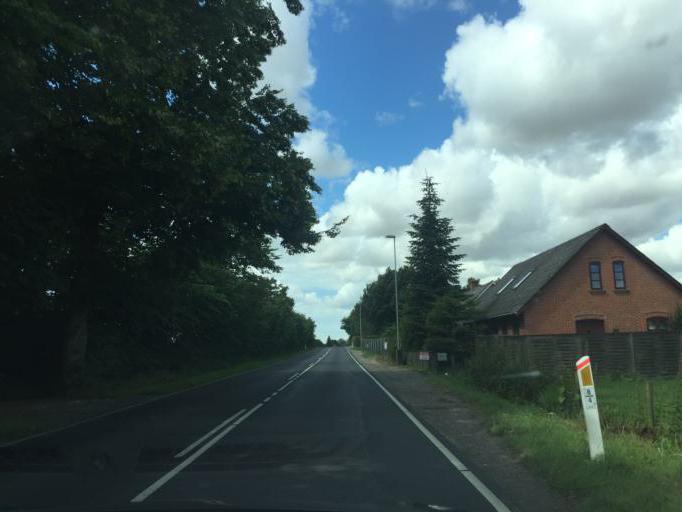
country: DK
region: South Denmark
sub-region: Odense Kommune
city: Stige
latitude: 55.4597
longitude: 10.3593
